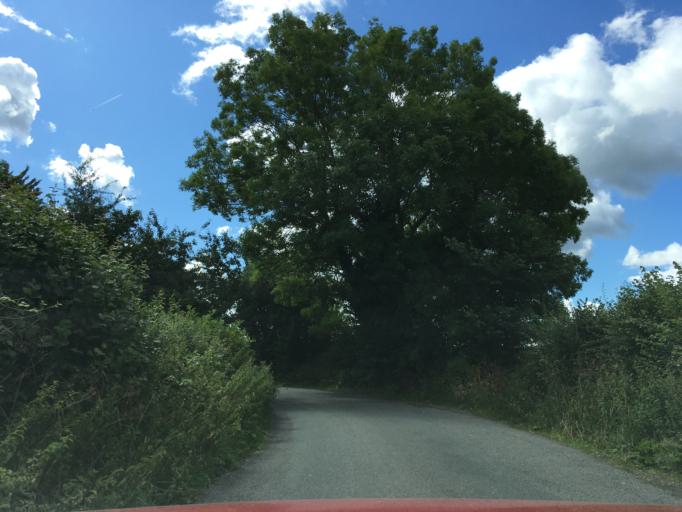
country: GB
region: England
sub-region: Gloucestershire
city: Newent
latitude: 51.8499
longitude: -2.3516
